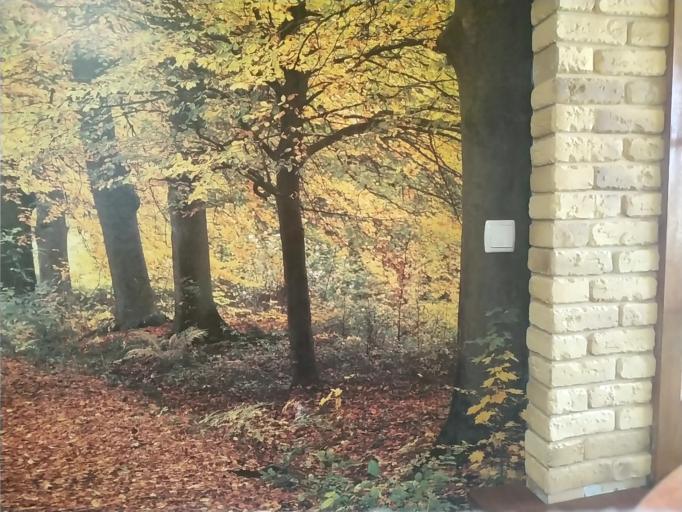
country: RU
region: Tverskaya
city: Vyshniy Volochek
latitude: 57.6675
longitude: 34.5325
